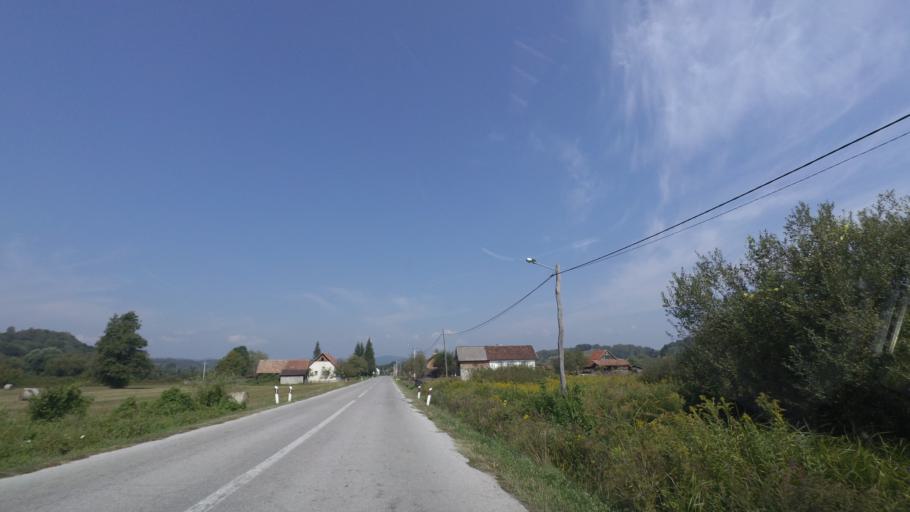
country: HR
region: Sisacko-Moslavacka
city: Dvor
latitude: 45.0933
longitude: 16.2975
